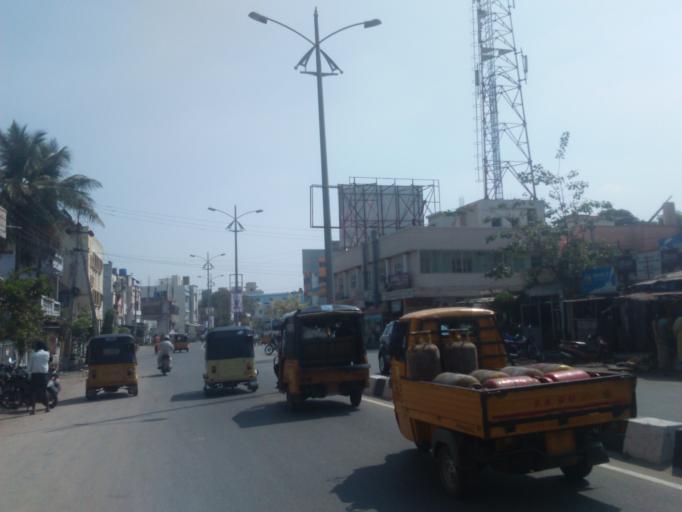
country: IN
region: Telangana
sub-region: Mahbubnagar
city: Alampur
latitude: 15.8395
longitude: 78.0386
